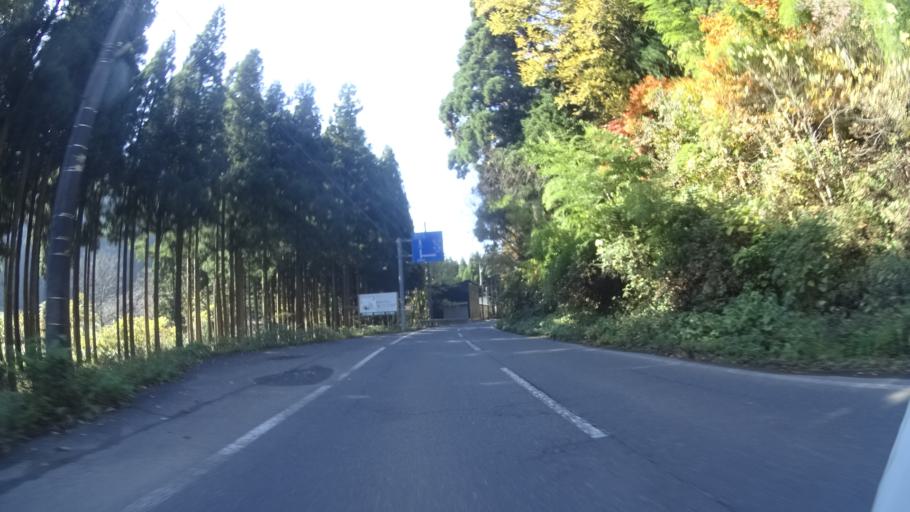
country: JP
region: Fukui
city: Ono
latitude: 35.8772
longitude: 136.3529
